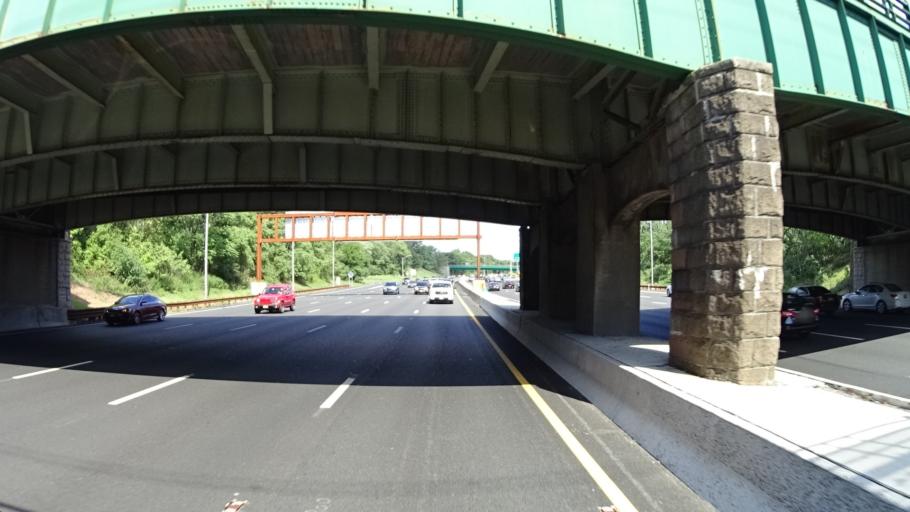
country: US
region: New Jersey
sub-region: Middlesex County
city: Iselin
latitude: 40.5701
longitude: -74.3279
